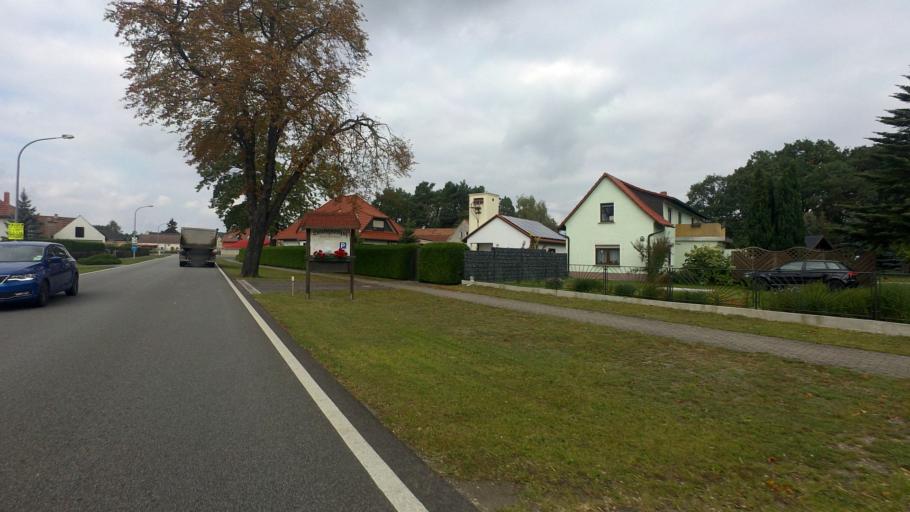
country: DE
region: Brandenburg
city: Bad Liebenwerda
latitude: 51.5467
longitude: 13.3861
